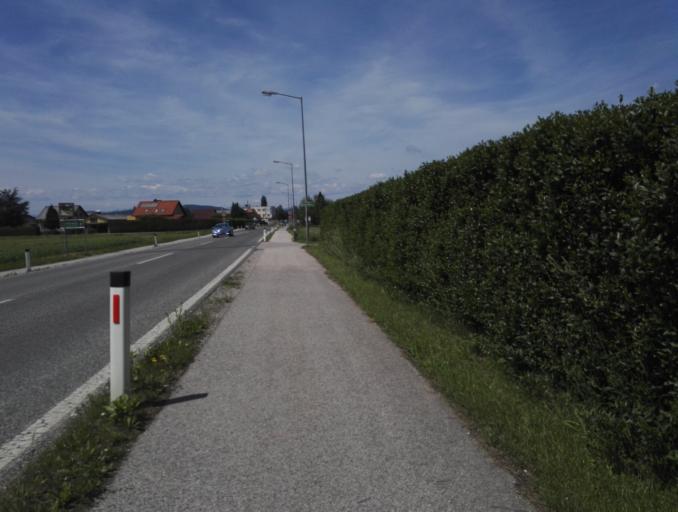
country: AT
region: Styria
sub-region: Politischer Bezirk Graz-Umgebung
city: Gossendorf
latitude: 46.9820
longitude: 15.4639
